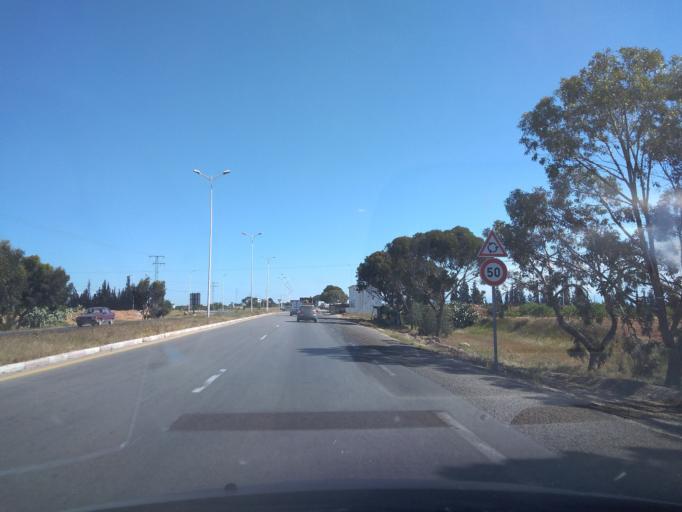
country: TN
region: Safaqis
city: Sfax
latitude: 34.8303
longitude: 10.7242
